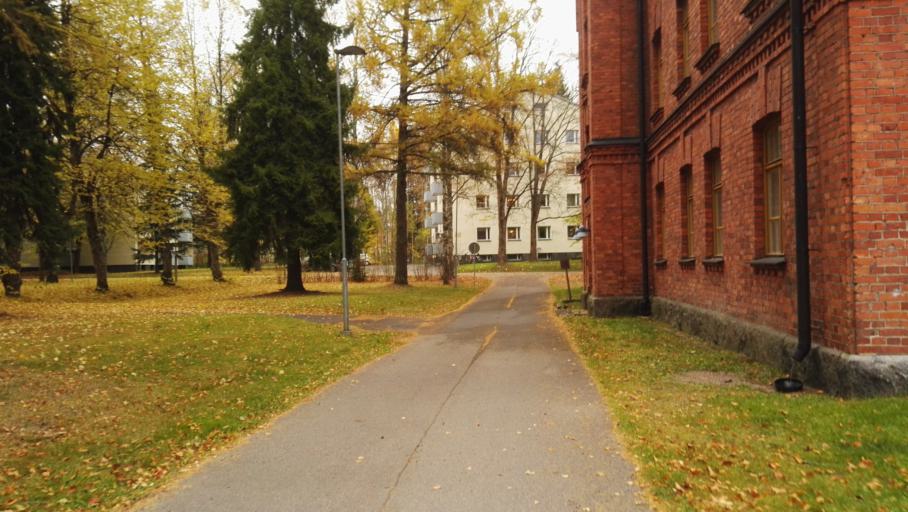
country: FI
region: Paijanne Tavastia
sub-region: Lahti
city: Lahti
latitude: 60.9710
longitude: 25.6280
